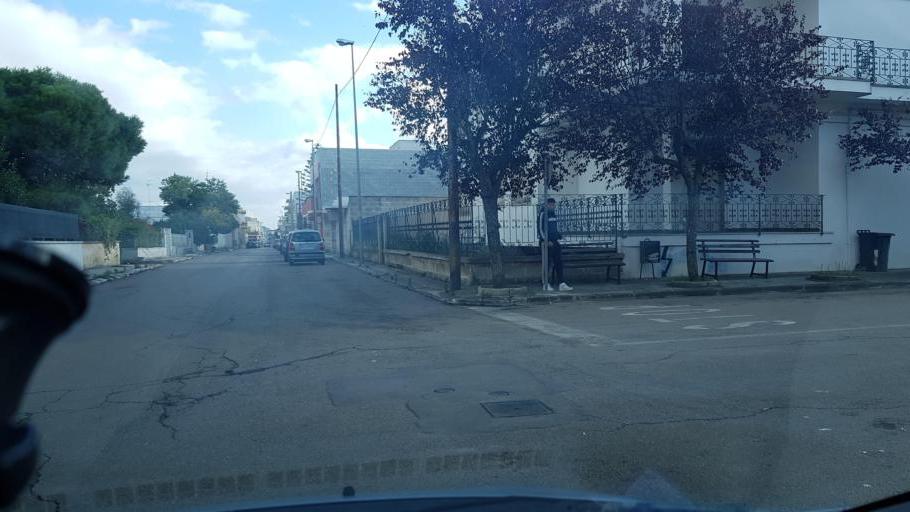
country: IT
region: Apulia
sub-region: Provincia di Lecce
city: Squinzano
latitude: 40.4374
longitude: 18.0346
